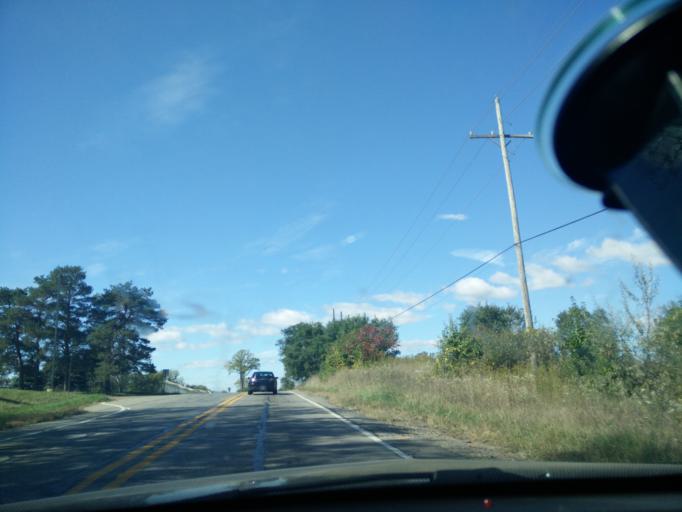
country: US
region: Michigan
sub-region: Wayne County
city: Northville
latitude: 42.3939
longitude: -83.5211
